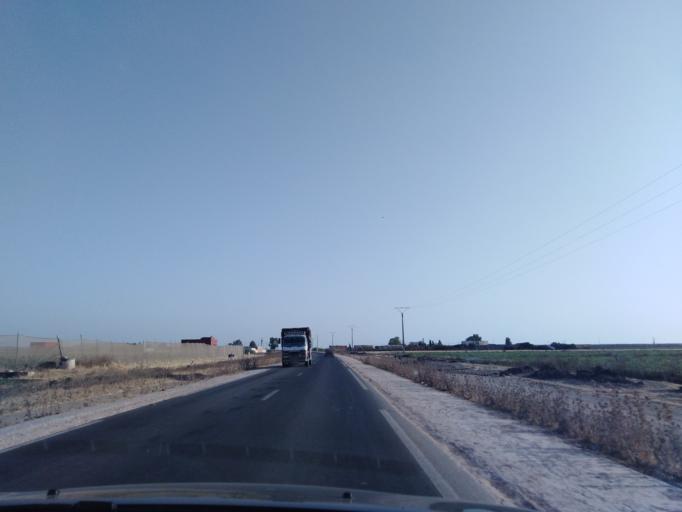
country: MA
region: Doukkala-Abda
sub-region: El-Jadida
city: Sidi Bennour
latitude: 32.5235
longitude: -8.7400
